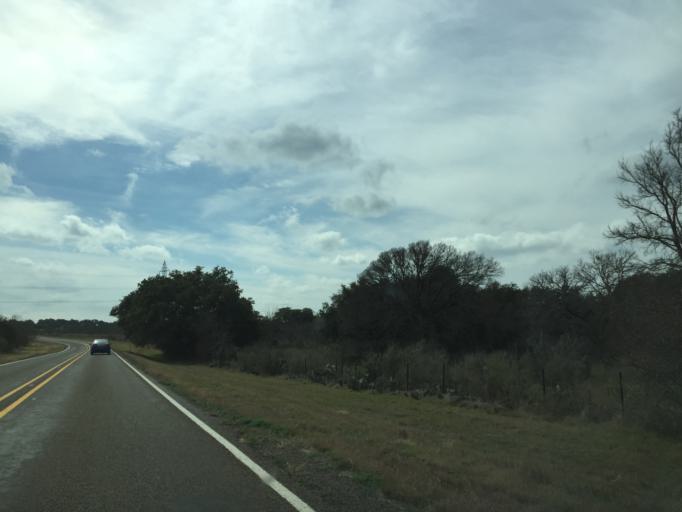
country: US
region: Texas
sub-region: Burnet County
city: Granite Shoals
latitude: 30.5262
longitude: -98.4471
